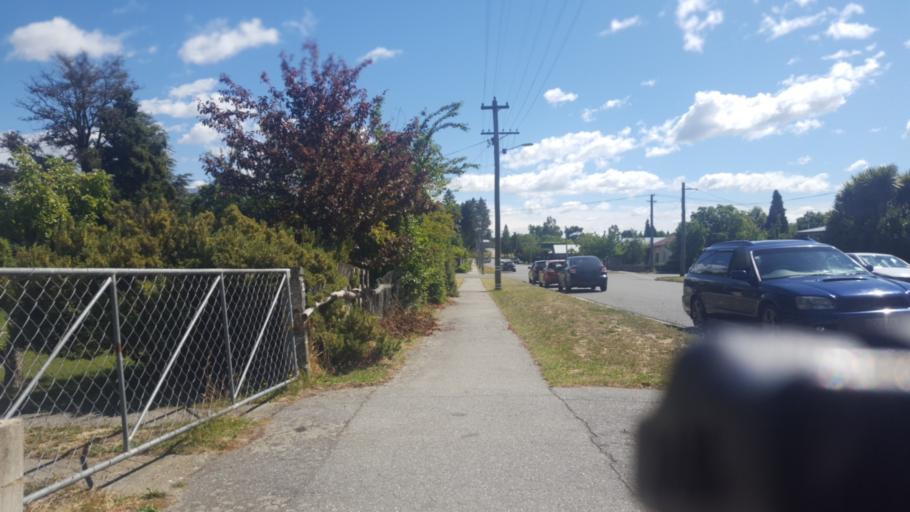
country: NZ
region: Otago
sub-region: Queenstown-Lakes District
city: Wanaka
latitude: -45.0457
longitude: 169.2085
